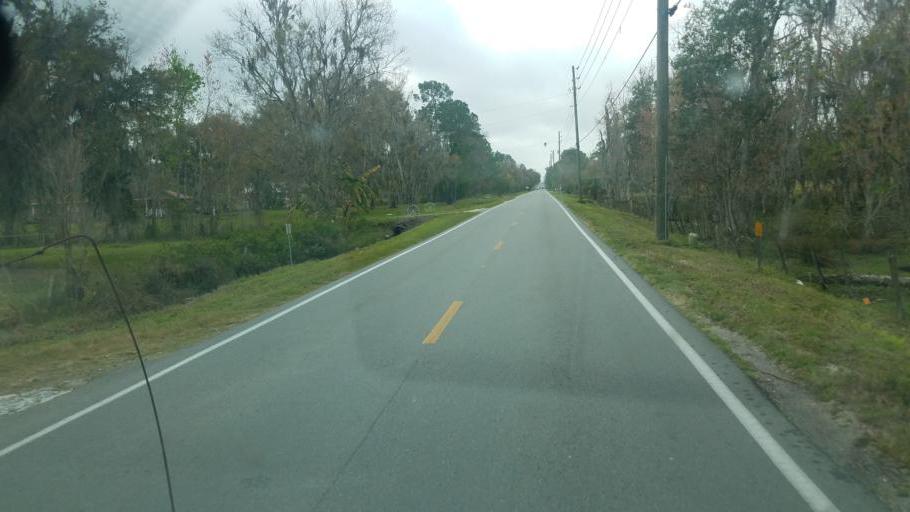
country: US
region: Florida
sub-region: Polk County
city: Kathleen
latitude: 28.1523
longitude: -82.0233
